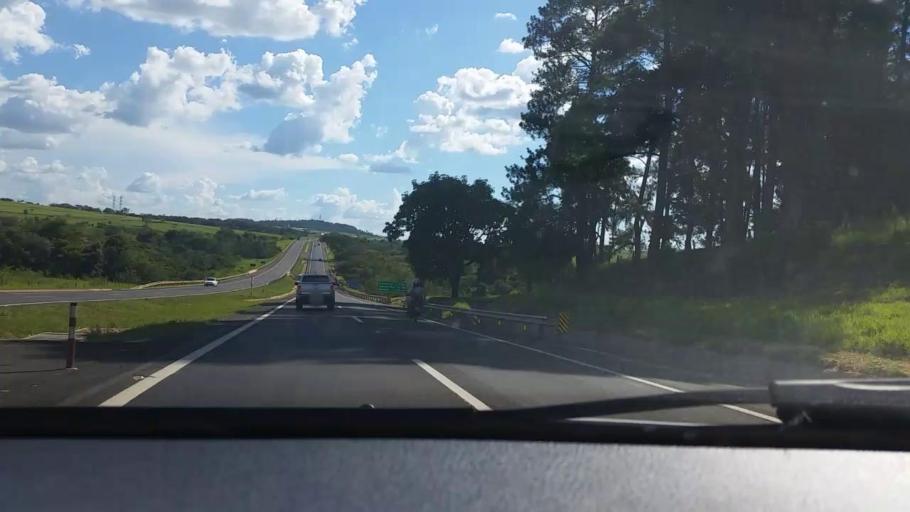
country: BR
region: Sao Paulo
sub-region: Bauru
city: Bauru
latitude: -22.4049
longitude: -49.0955
